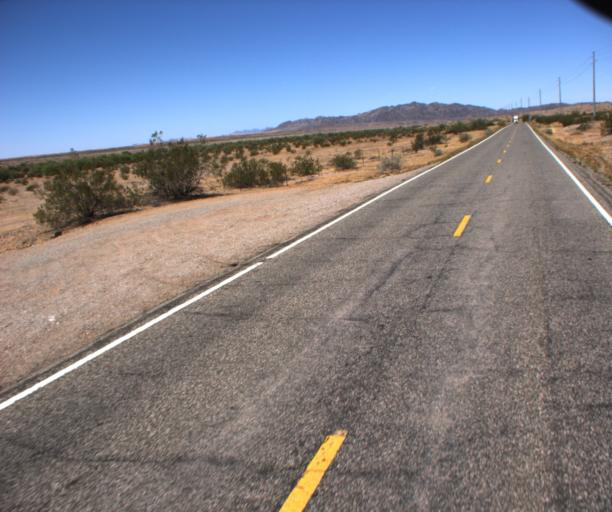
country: US
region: Arizona
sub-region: La Paz County
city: Parker
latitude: 33.9955
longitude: -114.1806
